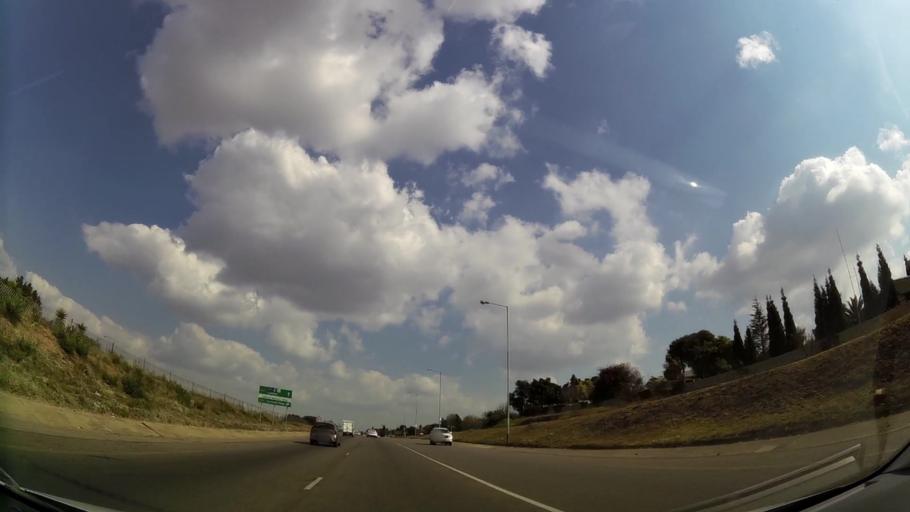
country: ZA
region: Gauteng
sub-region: City of Tshwane Metropolitan Municipality
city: Centurion
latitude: -25.8132
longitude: 28.2796
